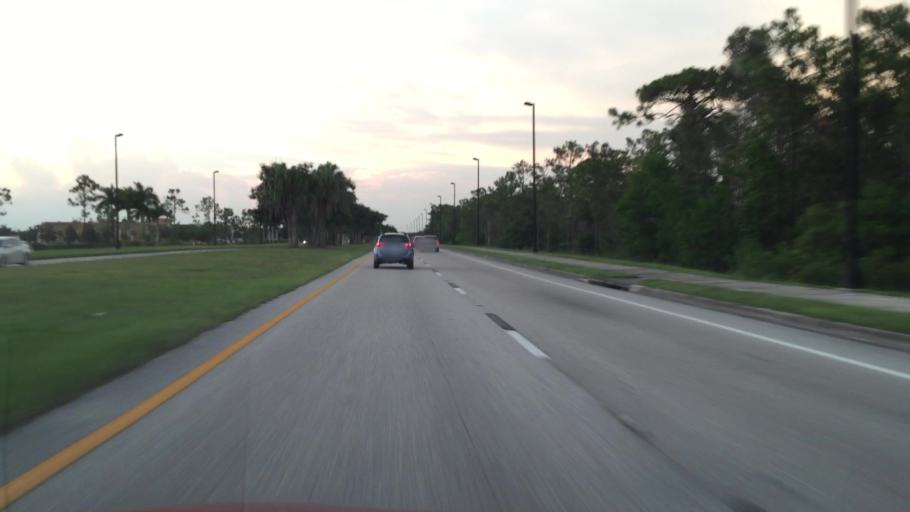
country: US
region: Florida
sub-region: Lee County
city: Gateway
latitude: 26.5312
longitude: -81.7856
